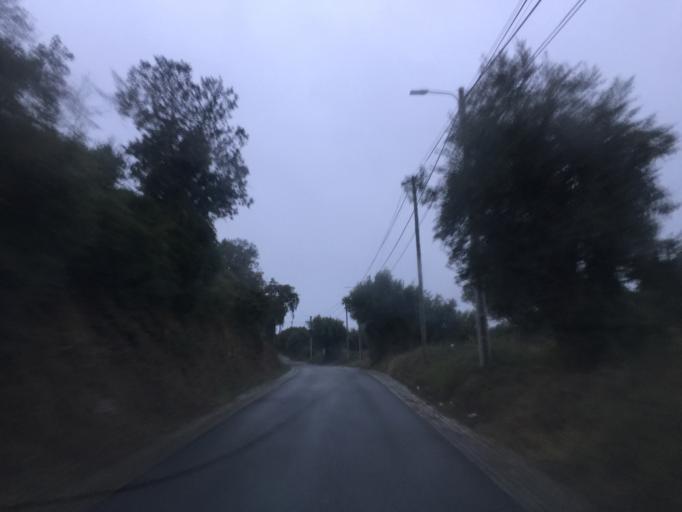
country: PT
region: Portalegre
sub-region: Avis
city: Avis
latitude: 39.0533
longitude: -7.8984
